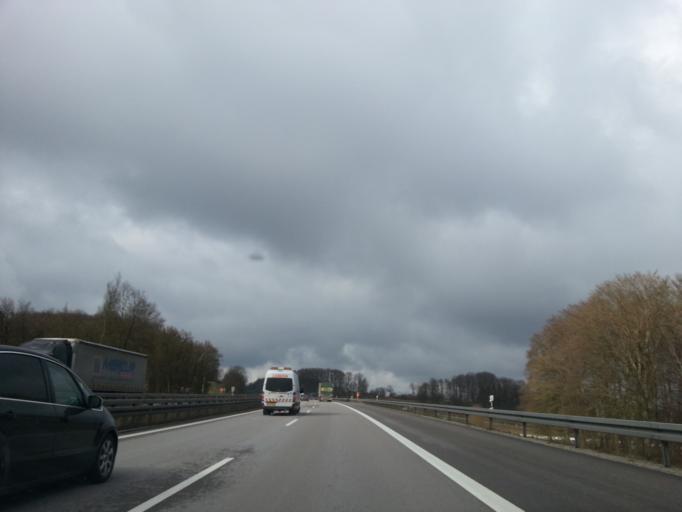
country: DE
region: Bavaria
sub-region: Upper Palatinate
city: Brunn
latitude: 49.1282
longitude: 11.8702
